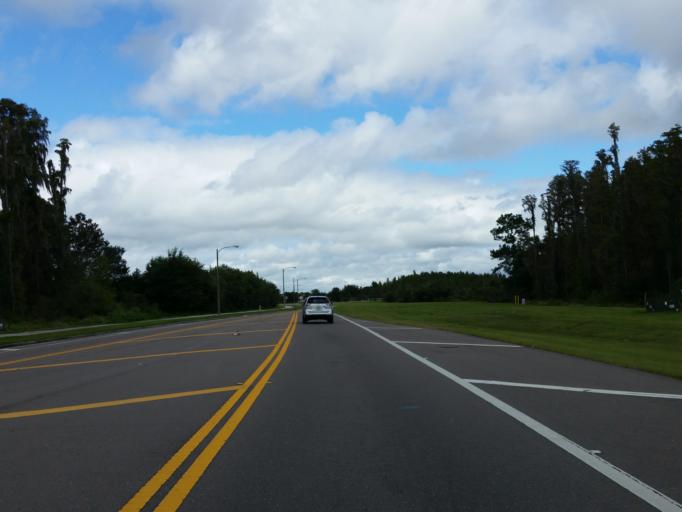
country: US
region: Florida
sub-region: Pasco County
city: Wesley Chapel
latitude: 28.2005
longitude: -82.2988
